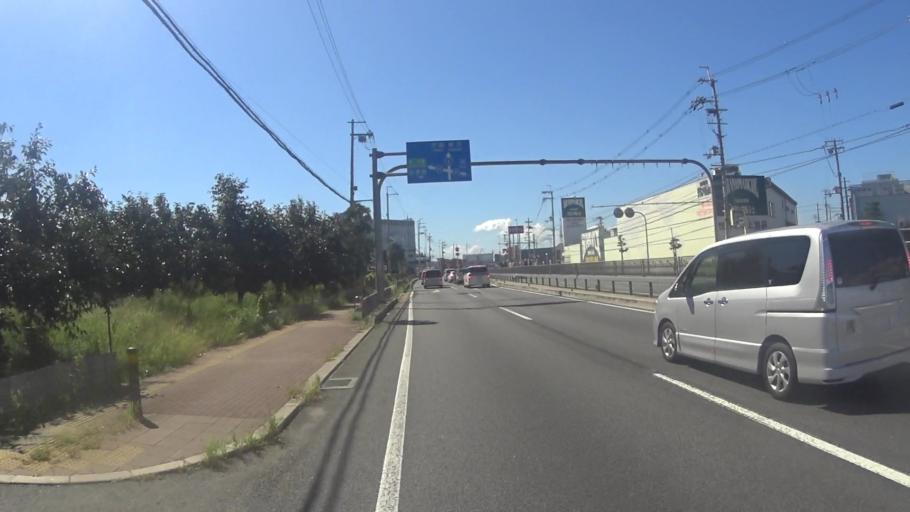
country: JP
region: Kyoto
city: Yawata
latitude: 34.8921
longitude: 135.7440
